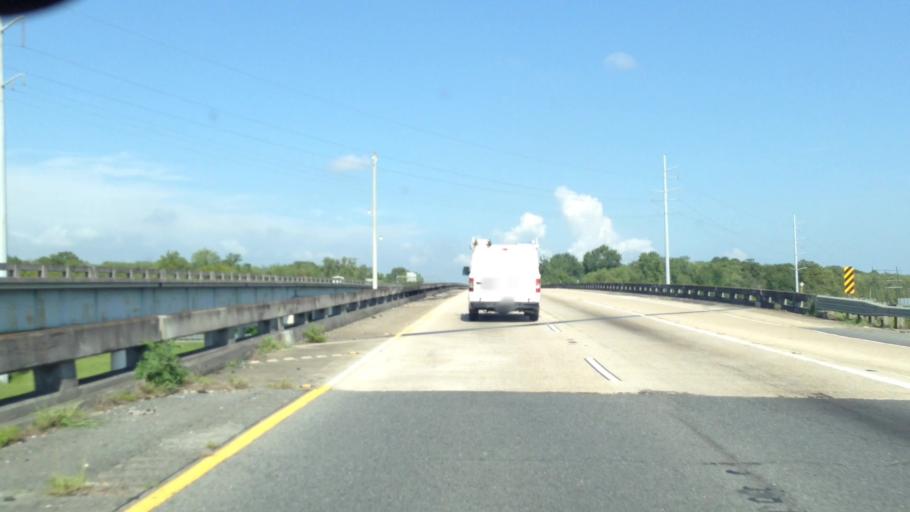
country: US
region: Louisiana
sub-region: Ascension Parish
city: Sorrento
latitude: 30.1535
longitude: -90.8050
